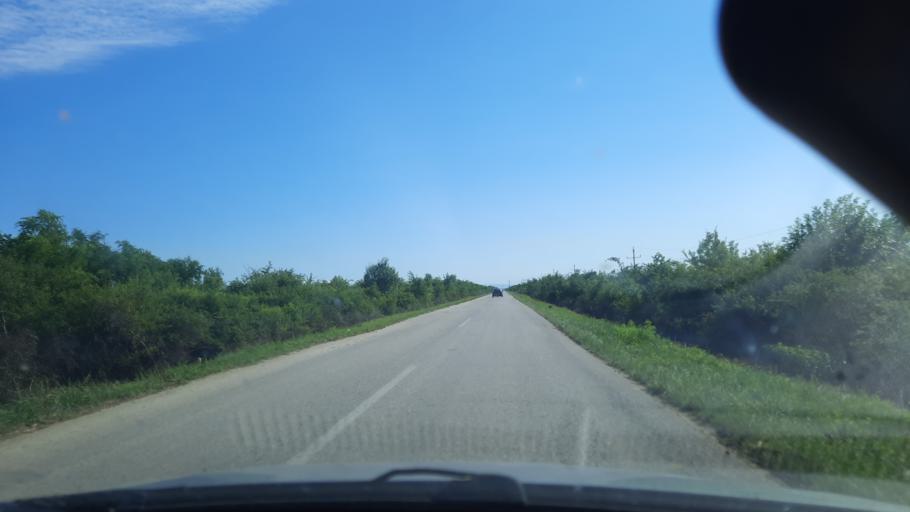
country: RS
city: Simanovci
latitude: 44.8008
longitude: 20.0968
